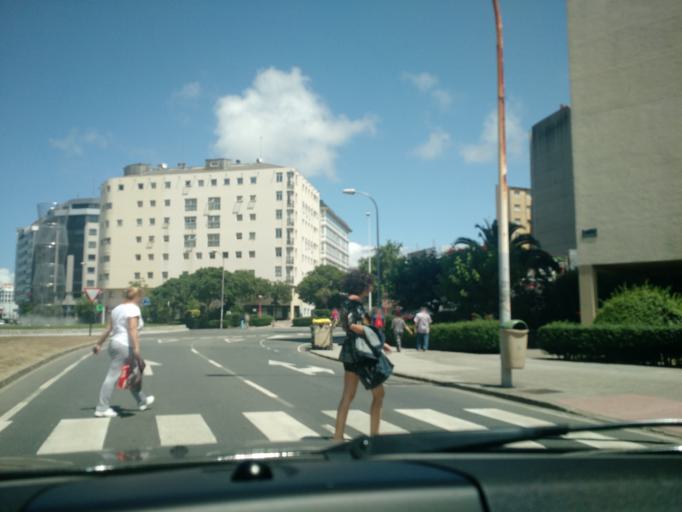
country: ES
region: Galicia
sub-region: Provincia da Coruna
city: A Coruna
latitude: 43.3498
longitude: -8.4049
